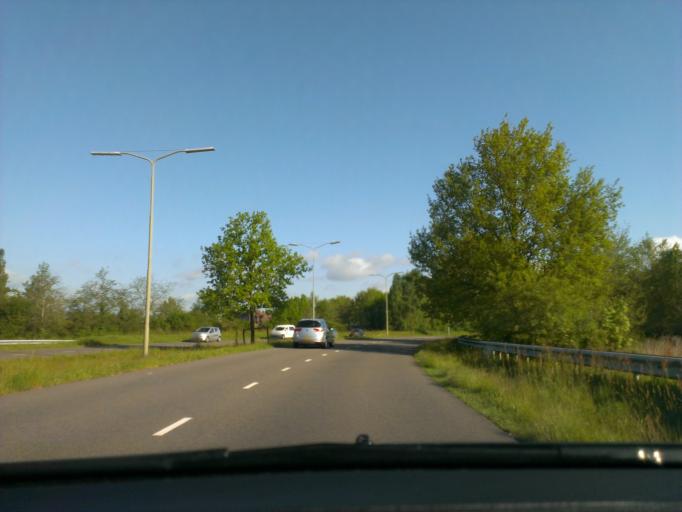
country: NL
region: Drenthe
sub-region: Gemeente Emmen
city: Emmen
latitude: 52.7652
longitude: 6.8967
